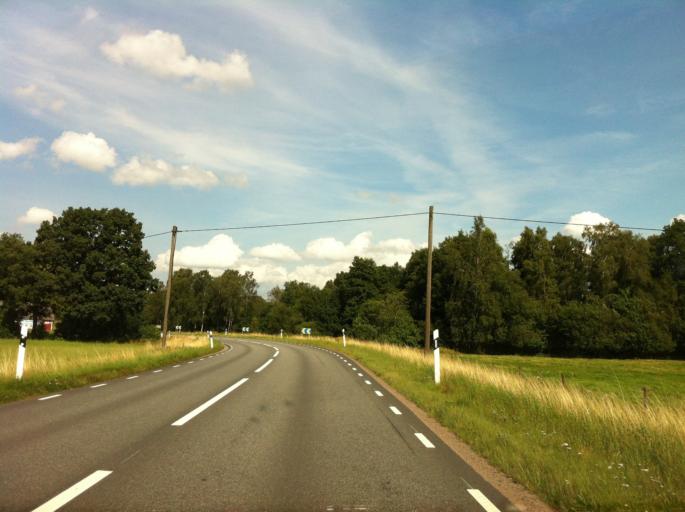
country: SE
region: Skane
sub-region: Klippans Kommun
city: Ljungbyhed
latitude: 55.9953
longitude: 13.2823
